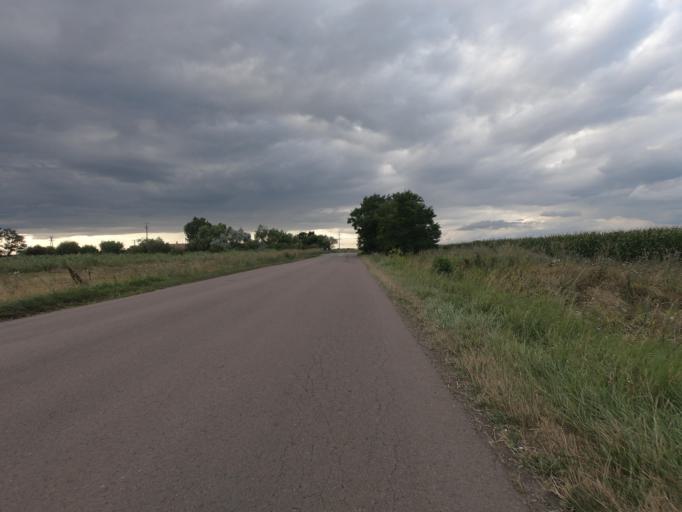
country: HU
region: Heves
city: Poroszlo
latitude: 47.6779
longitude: 20.6535
